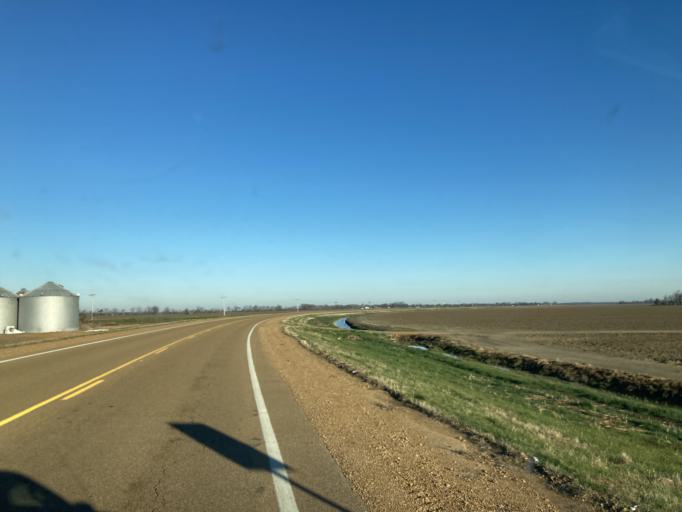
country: US
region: Mississippi
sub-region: Yazoo County
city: Yazoo City
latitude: 32.9305
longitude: -90.5859
